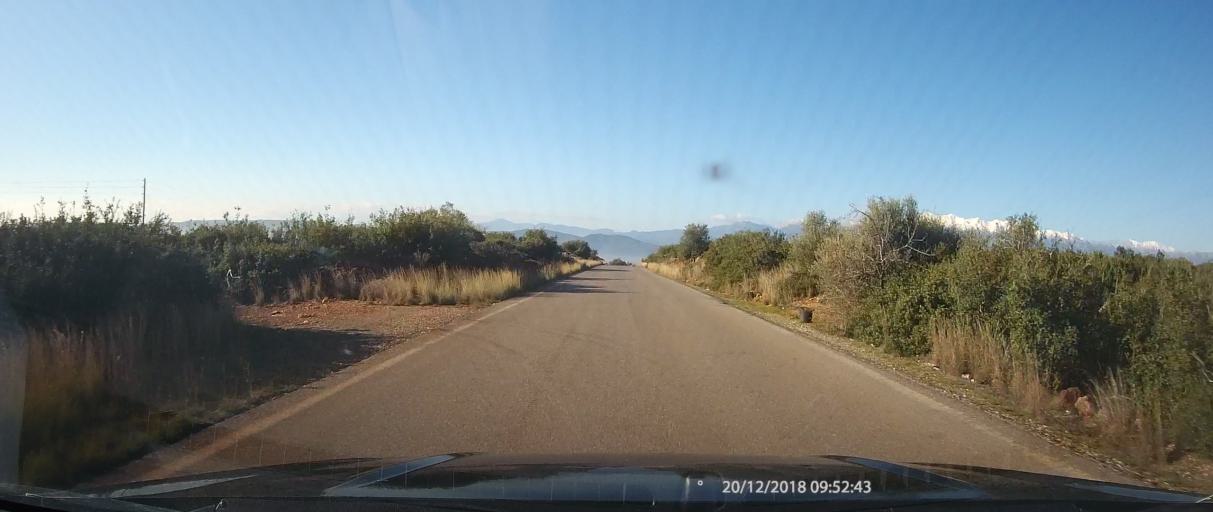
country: GR
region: Peloponnese
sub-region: Nomos Lakonias
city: Yerakion
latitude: 37.0090
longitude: 22.6406
